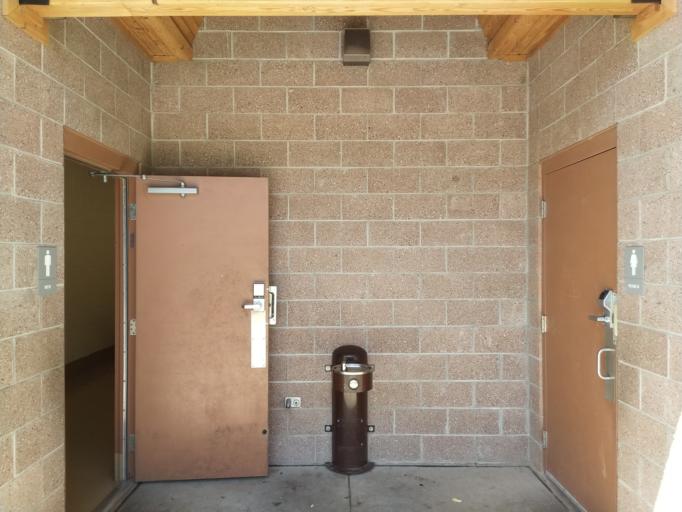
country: US
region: Colorado
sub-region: Mesa County
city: Grand Junction
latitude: 39.0741
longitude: -108.5506
